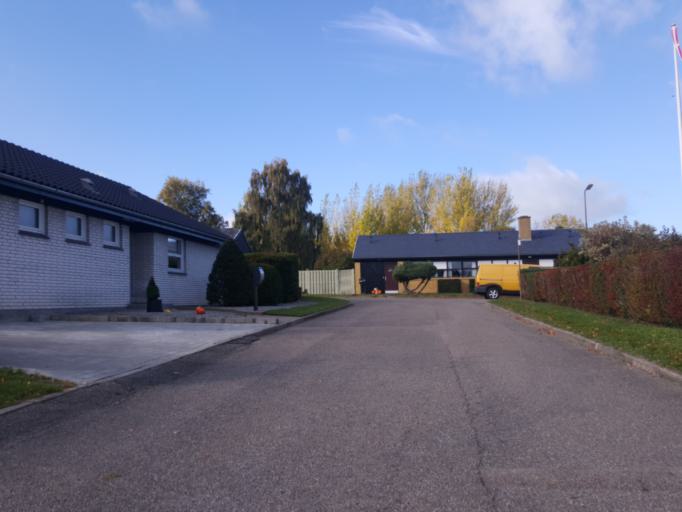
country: DK
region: Zealand
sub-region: Kalundborg Kommune
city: Kalundborg
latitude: 55.6912
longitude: 11.0741
